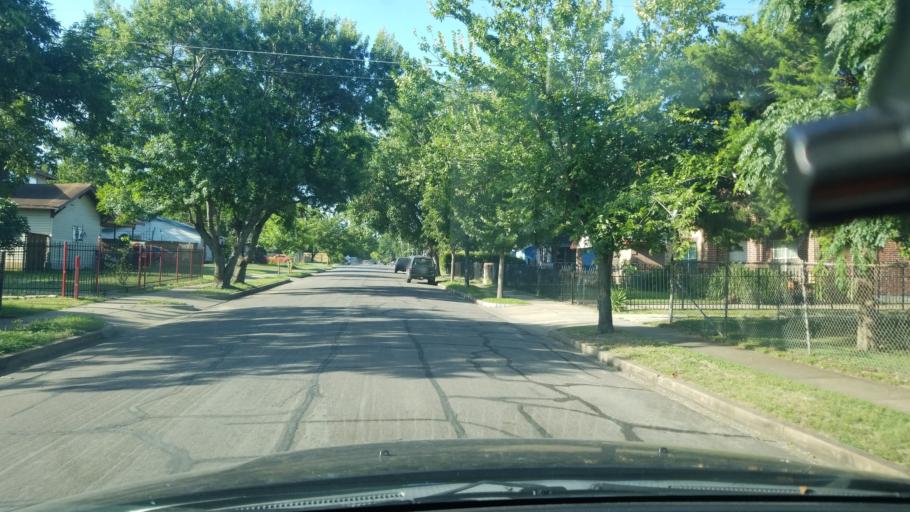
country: US
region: Texas
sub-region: Dallas County
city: Dallas
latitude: 32.7224
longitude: -96.8132
